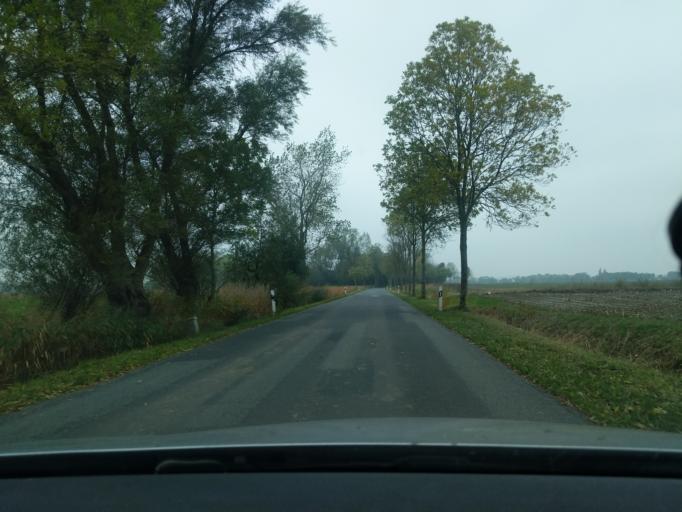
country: DE
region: Lower Saxony
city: Nordleda
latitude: 53.8254
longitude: 8.7923
